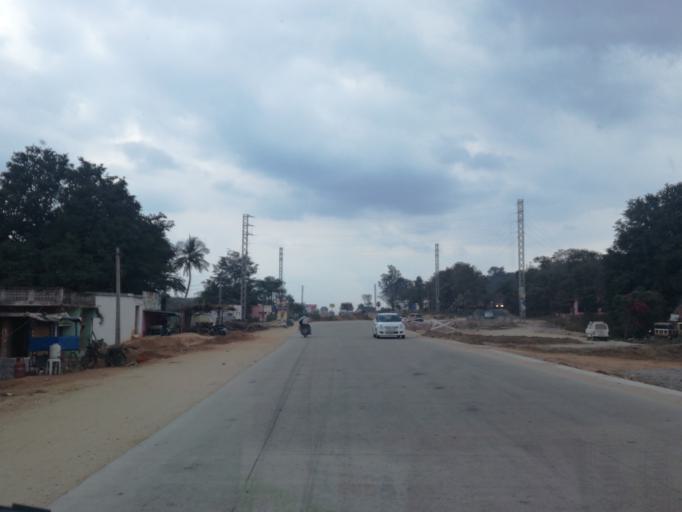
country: IN
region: Andhra Pradesh
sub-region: Chittoor
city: Ramapuram
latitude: 13.0924
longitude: 79.1338
